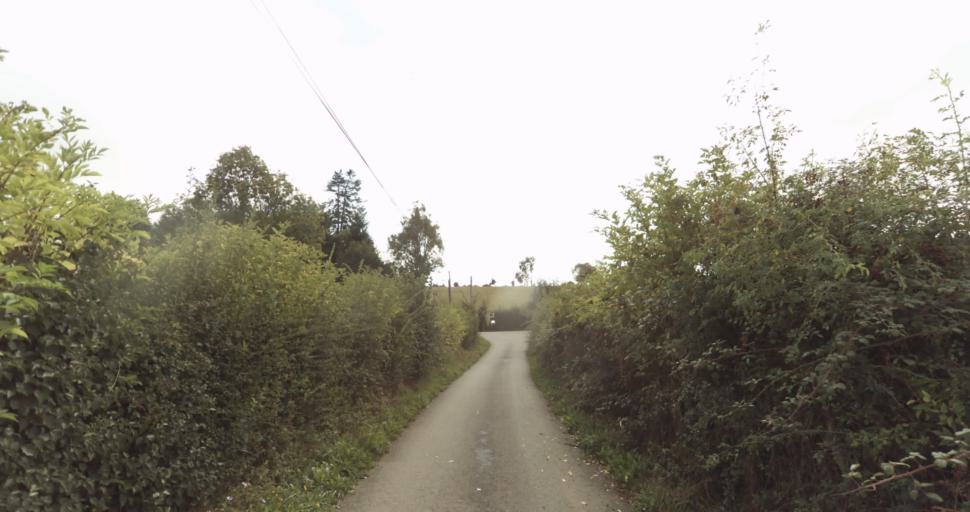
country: FR
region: Lower Normandy
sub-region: Departement de l'Orne
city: Gace
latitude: 48.8061
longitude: 0.2777
